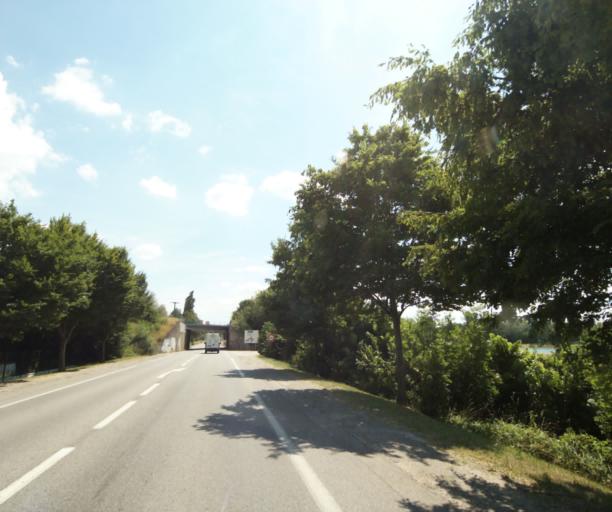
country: FR
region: Lorraine
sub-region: Departement de Meurthe-et-Moselle
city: Luneville
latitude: 48.5793
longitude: 6.4813
